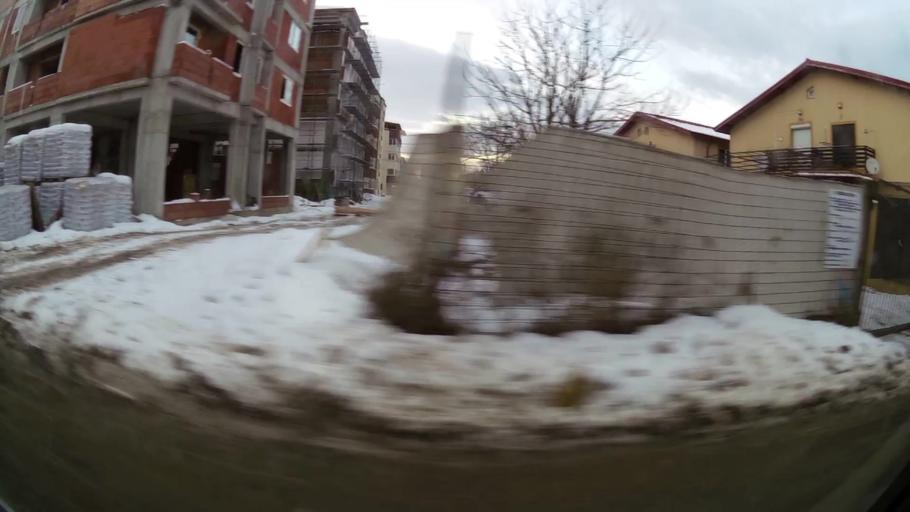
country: RO
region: Ilfov
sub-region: Comuna Popesti-Leordeni
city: Popesti-Leordeni
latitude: 44.3682
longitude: 26.1549
